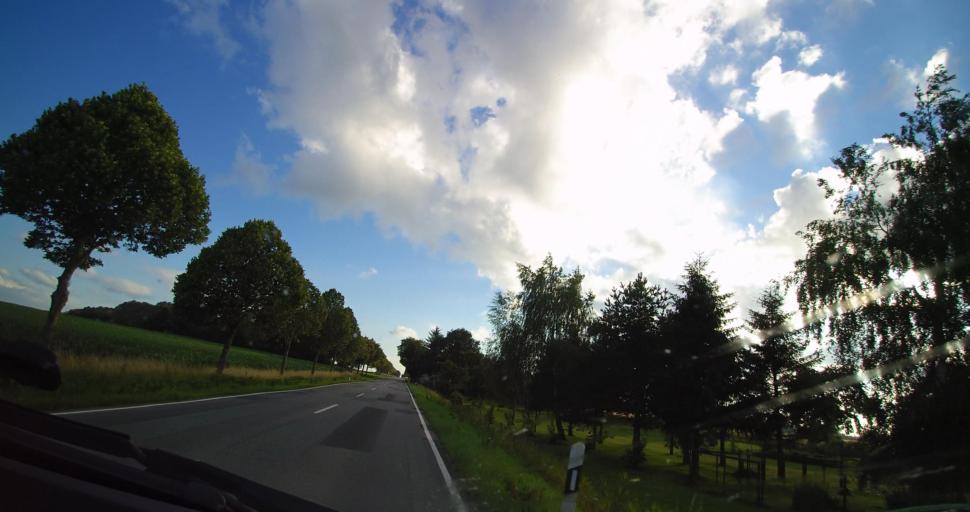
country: DE
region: Mecklenburg-Vorpommern
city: Franzburg
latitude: 54.1863
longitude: 12.8573
